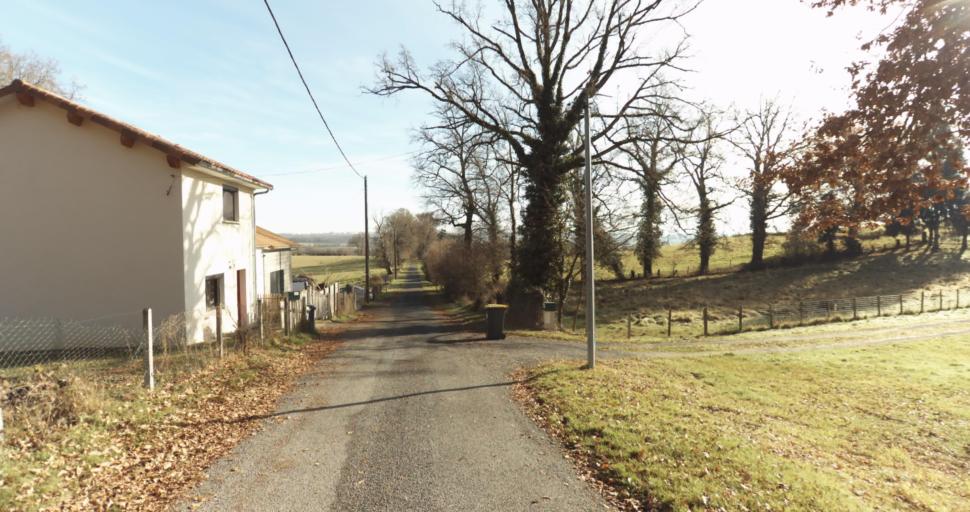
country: FR
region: Limousin
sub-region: Departement de la Haute-Vienne
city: Aixe-sur-Vienne
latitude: 45.7787
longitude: 1.1191
